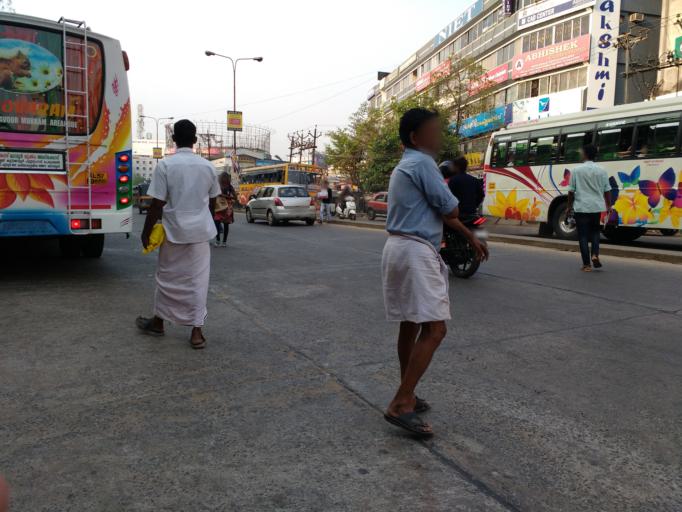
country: IN
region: Kerala
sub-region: Kozhikode
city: Kozhikode
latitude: 11.2572
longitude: 75.7865
